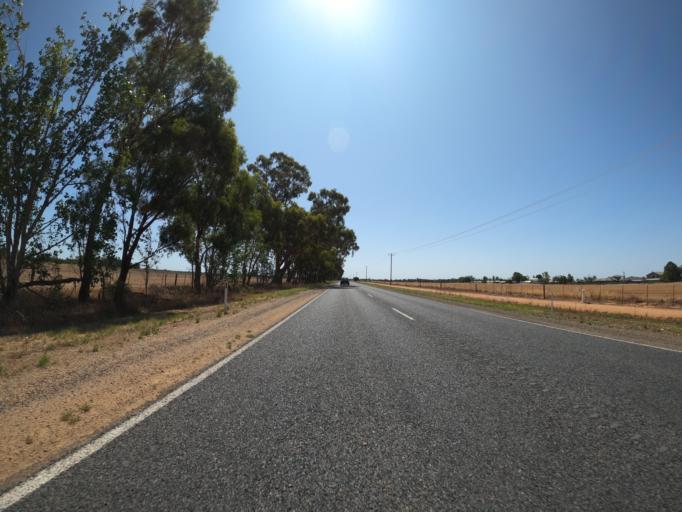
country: AU
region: Victoria
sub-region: Moira
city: Yarrawonga
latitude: -36.0233
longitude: 146.0623
